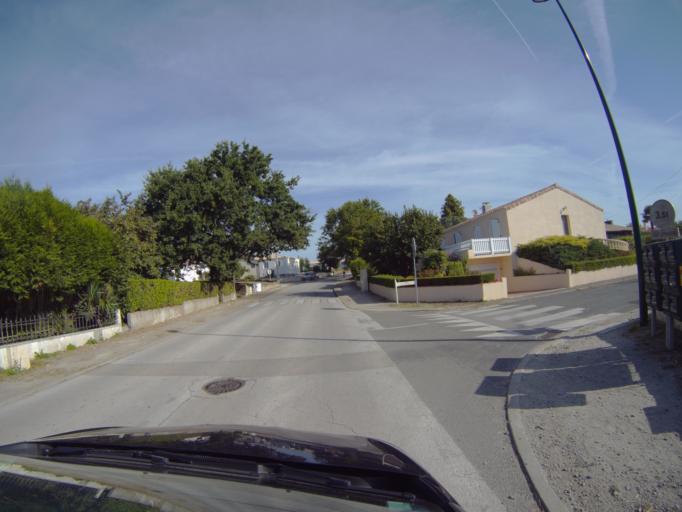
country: FR
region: Pays de la Loire
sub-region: Departement de la Vendee
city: Les Clouzeaux
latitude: 46.6343
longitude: -1.5099
